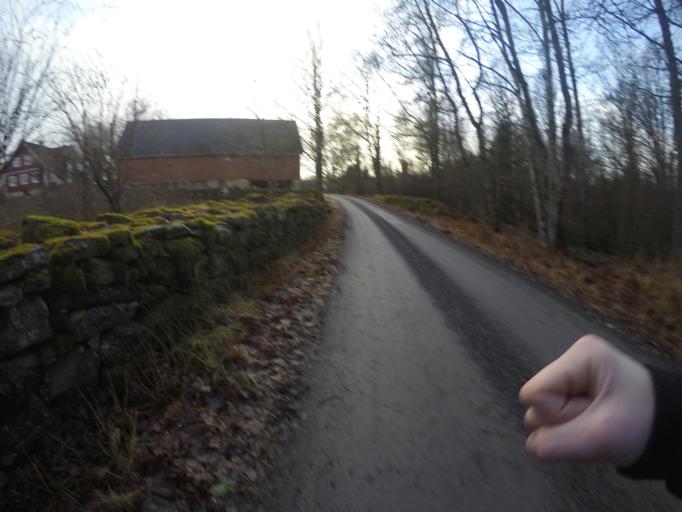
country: SE
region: Skane
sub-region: Osby Kommun
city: Lonsboda
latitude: 56.3786
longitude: 14.3381
